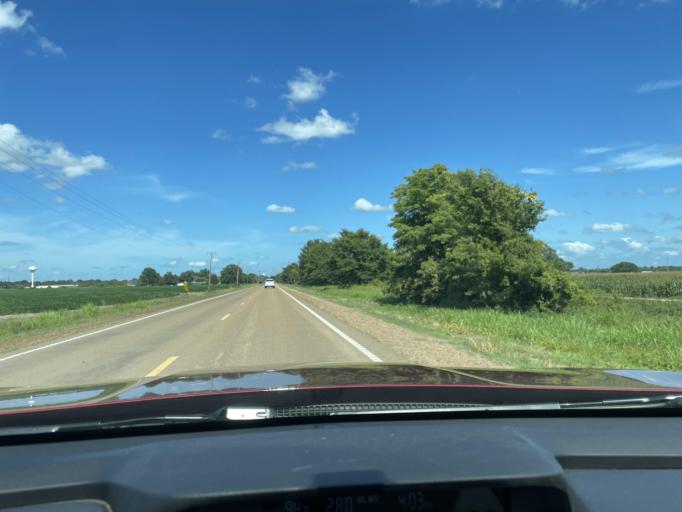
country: US
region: Mississippi
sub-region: Humphreys County
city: Belzoni
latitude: 33.1838
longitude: -90.5095
